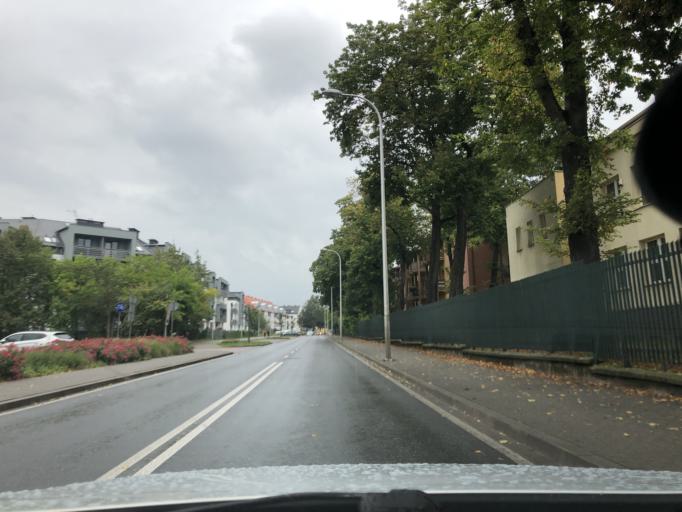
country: PL
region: Greater Poland Voivodeship
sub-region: Powiat pilski
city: Pila
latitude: 53.1537
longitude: 16.7622
